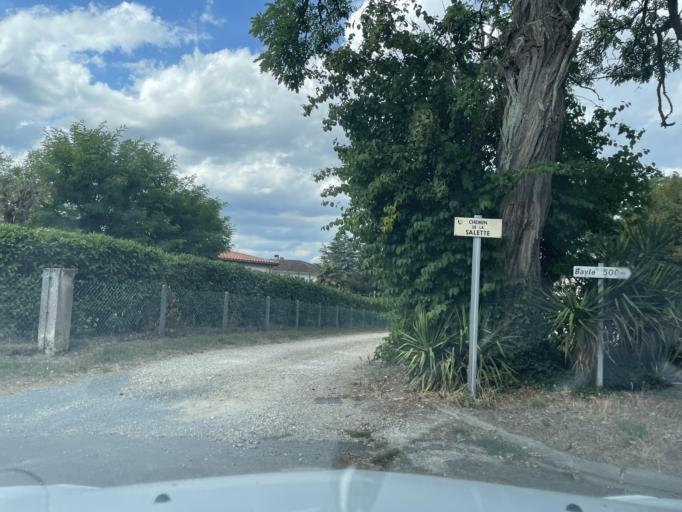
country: FR
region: Aquitaine
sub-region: Departement du Lot-et-Garonne
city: Casteljaloux
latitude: 44.3113
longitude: 0.1008
